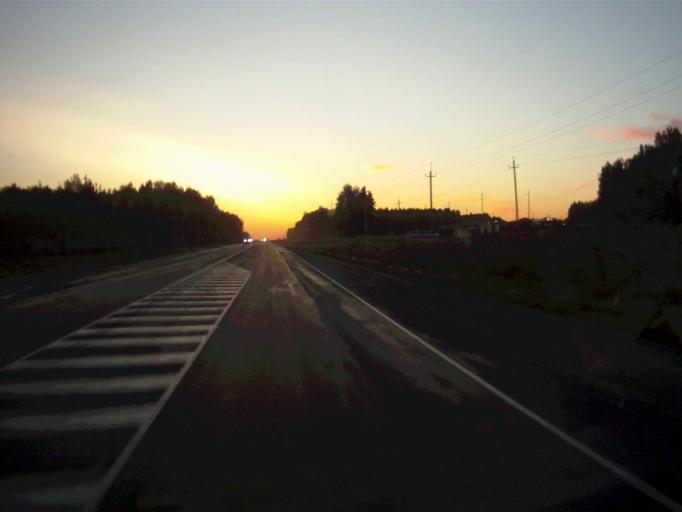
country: RU
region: Chelyabinsk
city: Poletayevo
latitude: 55.2197
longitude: 61.0289
